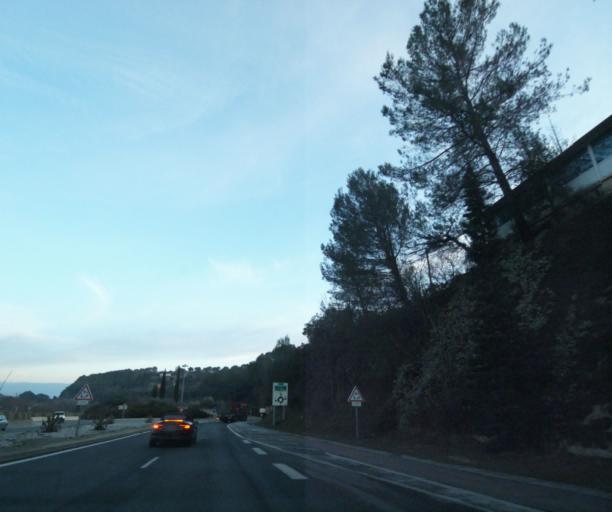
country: FR
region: Provence-Alpes-Cote d'Azur
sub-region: Departement du Var
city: Trans-en-Provence
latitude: 43.4957
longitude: 6.4925
